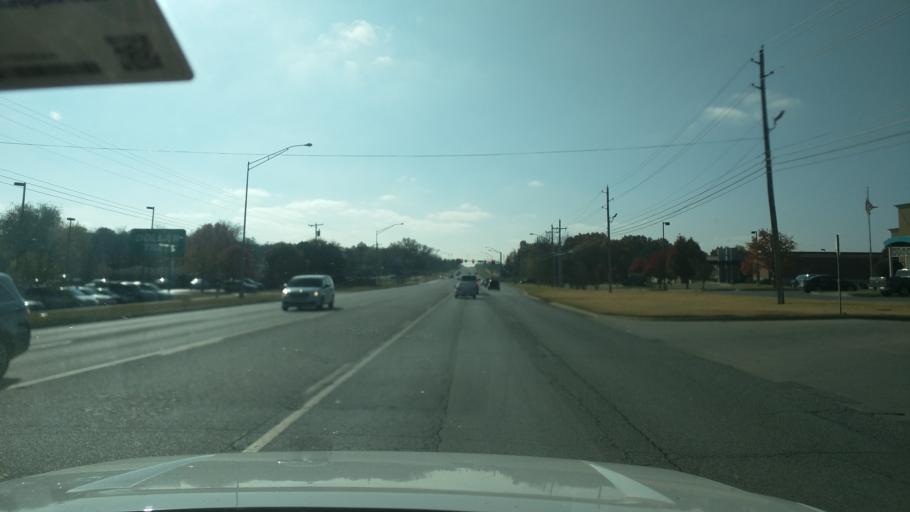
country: US
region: Oklahoma
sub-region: Washington County
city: Bartlesville
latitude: 36.7103
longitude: -95.9352
